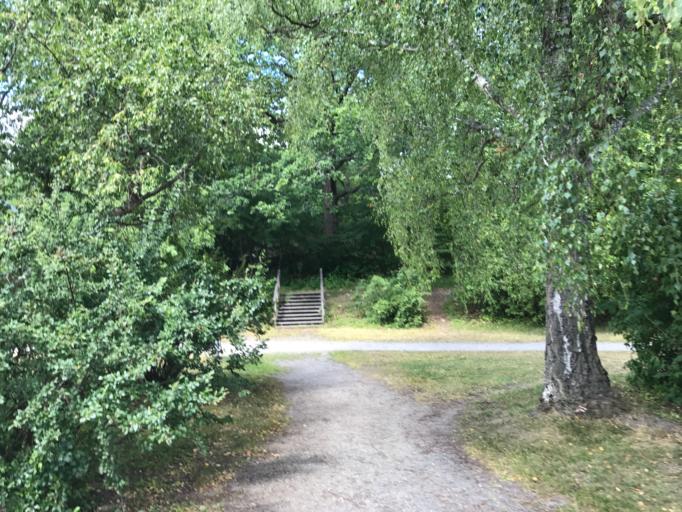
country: SE
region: Stockholm
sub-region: Huddinge Kommun
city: Segeltorp
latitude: 59.3017
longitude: 17.9698
